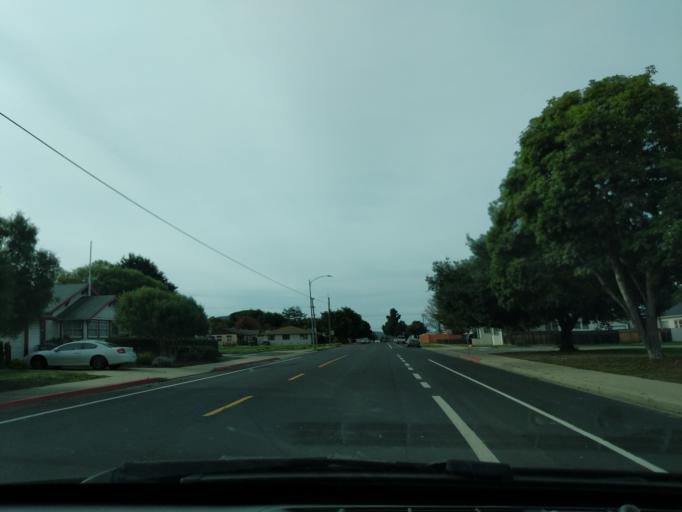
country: US
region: California
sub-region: Santa Barbara County
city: Lompoc
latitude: 34.6373
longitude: -120.4548
